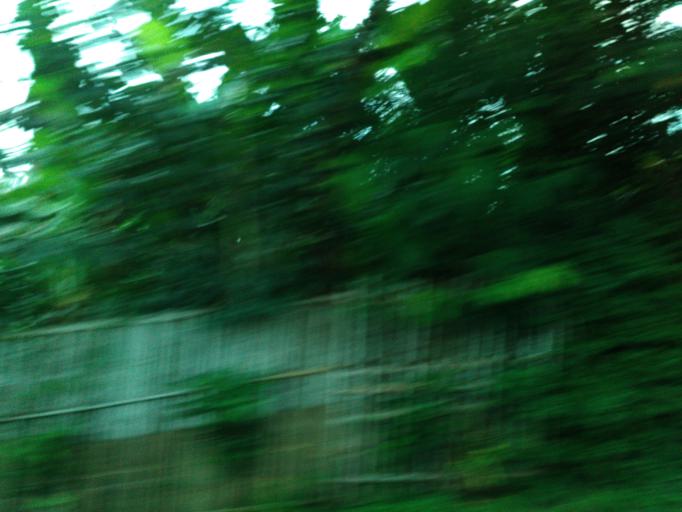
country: ID
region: Central Java
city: Ceper
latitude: -7.6569
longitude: 110.6946
